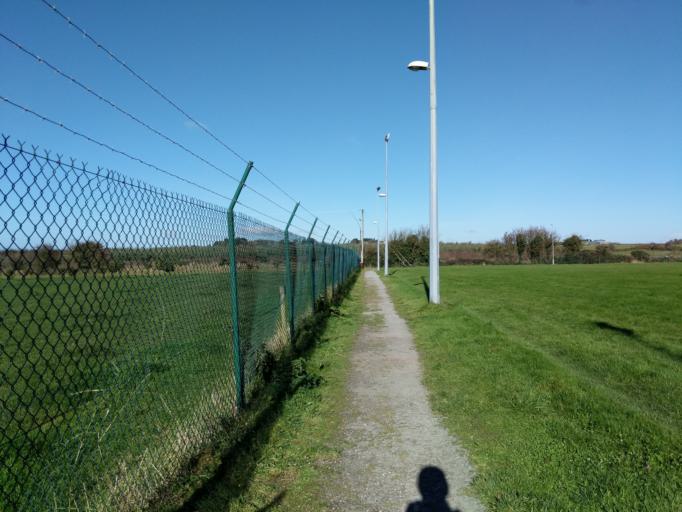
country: IE
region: Munster
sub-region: County Cork
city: Blarney
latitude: 51.9828
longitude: -8.5348
